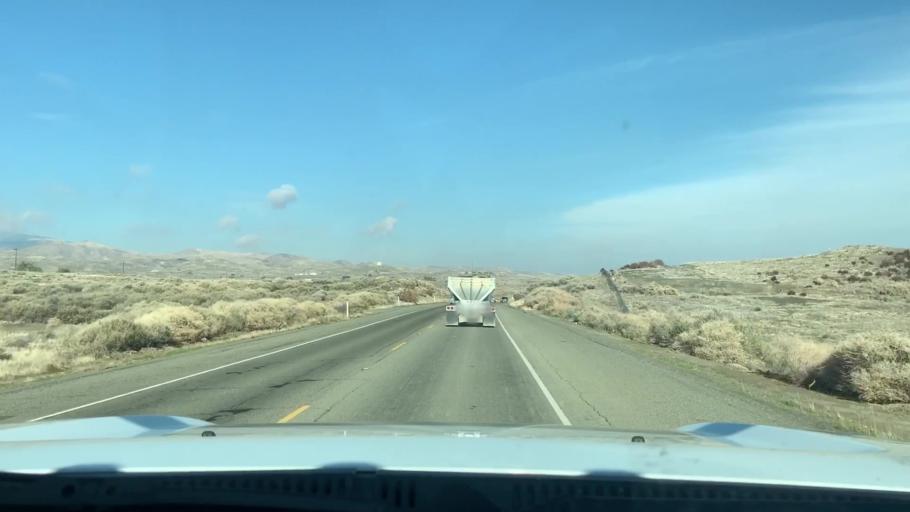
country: US
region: California
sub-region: Fresno County
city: Coalinga
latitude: 36.2258
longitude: -120.3131
